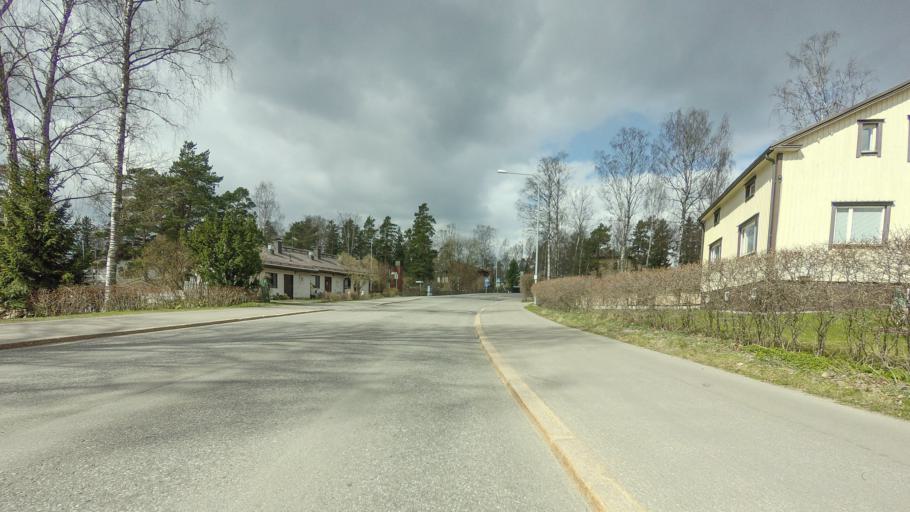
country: FI
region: Uusimaa
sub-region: Helsinki
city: Vantaa
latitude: 60.2200
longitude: 25.0982
